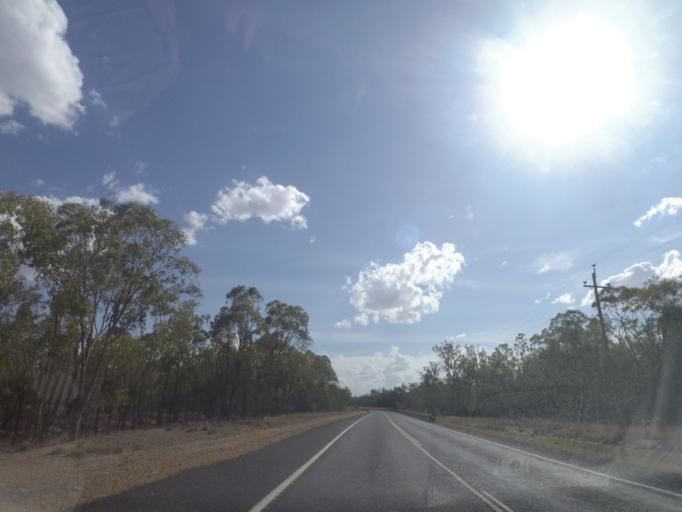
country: AU
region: New South Wales
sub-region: Moree Plains
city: Boggabilla
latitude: -28.5368
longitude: 150.8906
